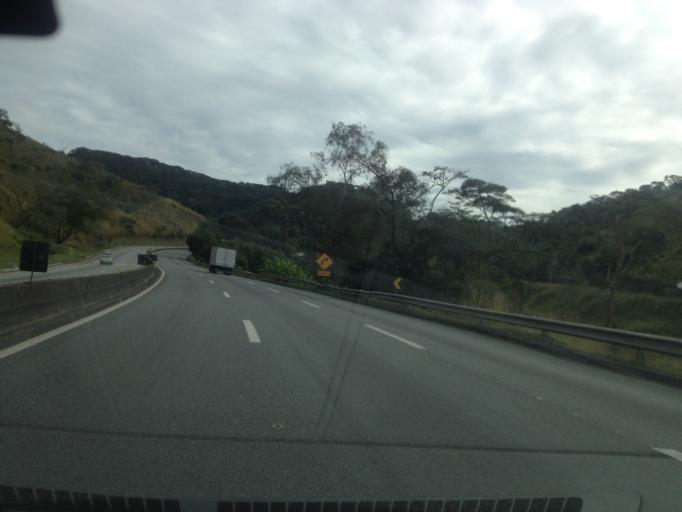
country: BR
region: Rio de Janeiro
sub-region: Pirai
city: Pirai
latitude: -22.6089
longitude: -43.9323
